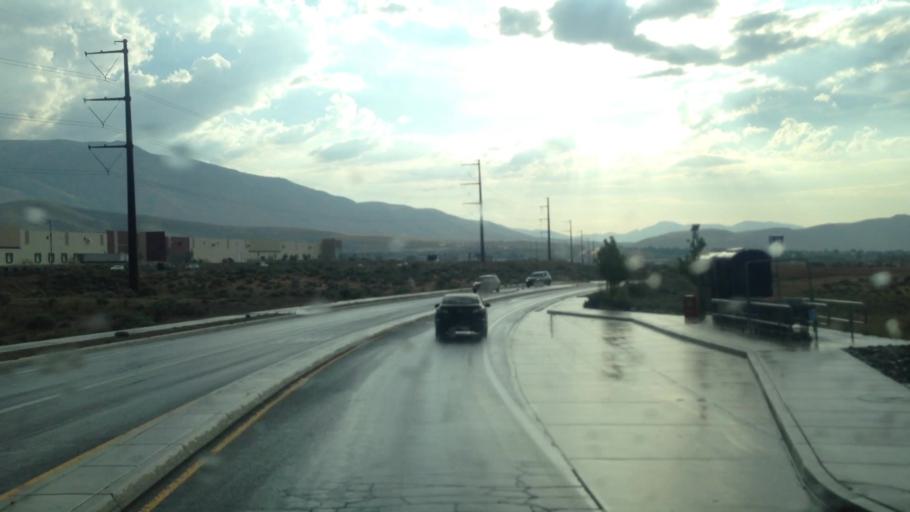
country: US
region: Nevada
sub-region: Washoe County
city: Lemmon Valley
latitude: 39.6145
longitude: -119.8552
